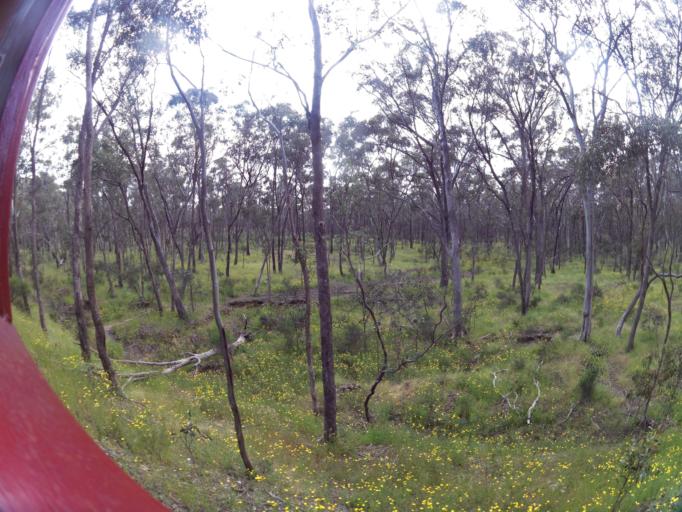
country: AU
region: Victoria
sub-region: Mount Alexander
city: Castlemaine
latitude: -37.0496
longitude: 144.1842
